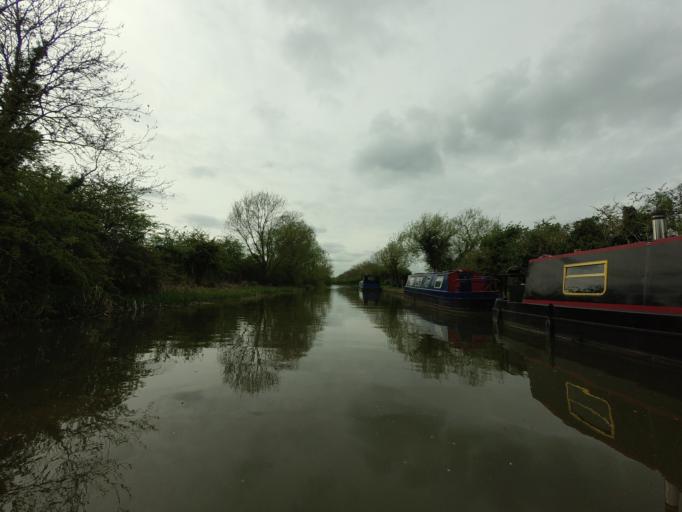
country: GB
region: England
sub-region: Milton Keynes
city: Bradwell
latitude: 52.0740
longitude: -0.7702
